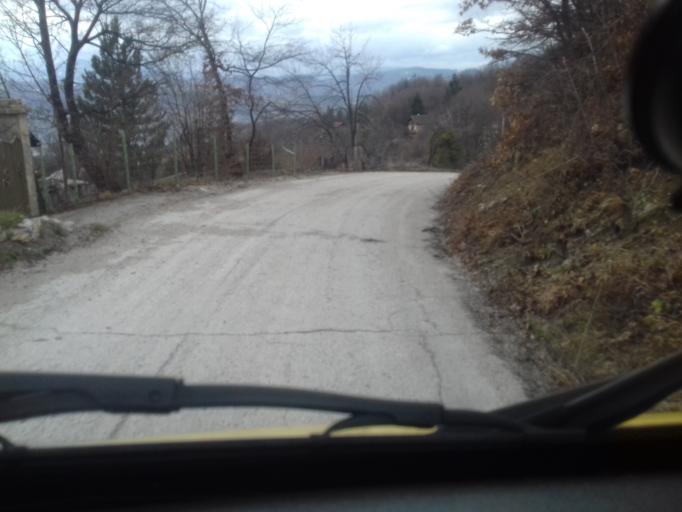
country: BA
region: Federation of Bosnia and Herzegovina
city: Zenica
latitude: 44.2269
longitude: 17.9519
